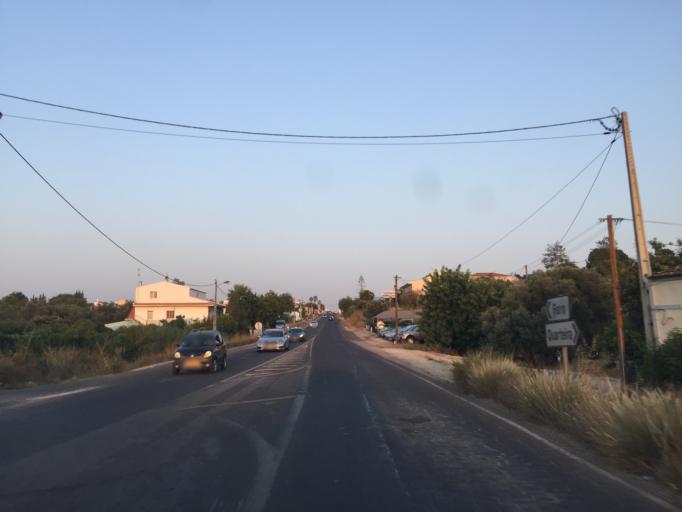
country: PT
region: Faro
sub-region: Loule
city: Almancil
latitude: 37.0802
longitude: -7.9991
